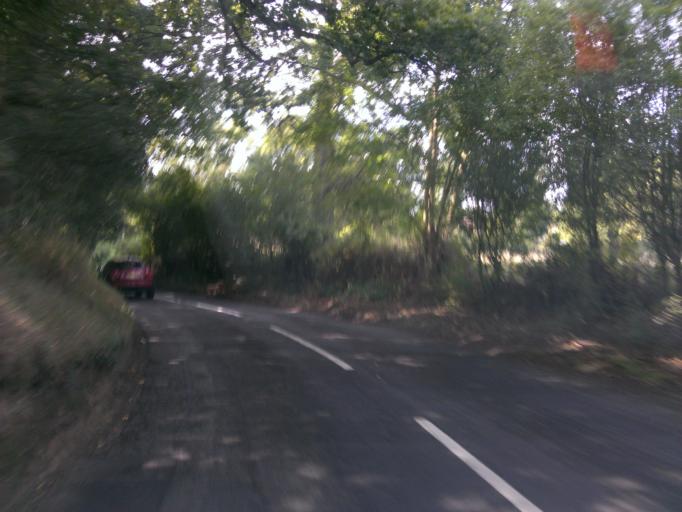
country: GB
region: England
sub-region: Kent
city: Edenbridge
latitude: 51.1954
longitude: 0.1102
